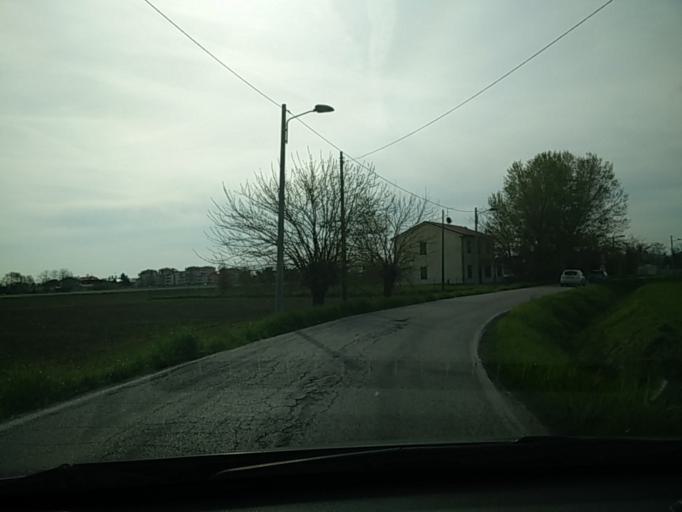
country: IT
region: Emilia-Romagna
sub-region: Provincia di Rimini
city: Santa Giustina
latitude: 44.0754
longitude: 12.5080
